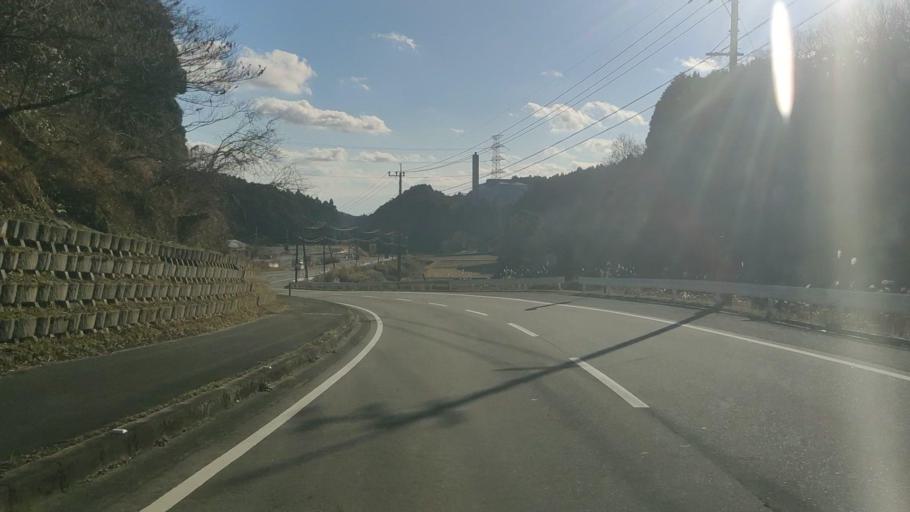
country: JP
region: Saga Prefecture
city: Kanzakimachi-kanzaki
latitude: 33.4030
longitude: 130.2725
